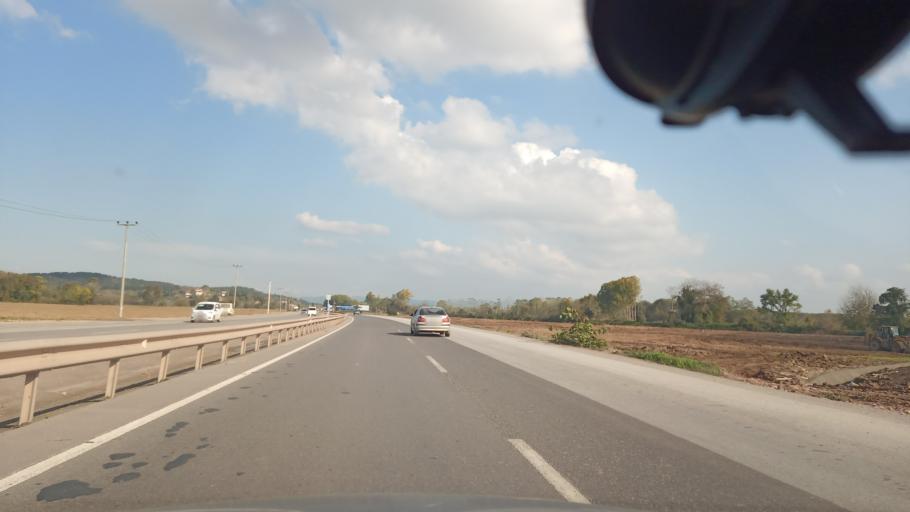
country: TR
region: Sakarya
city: Adapazari
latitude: 40.8241
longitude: 30.4640
